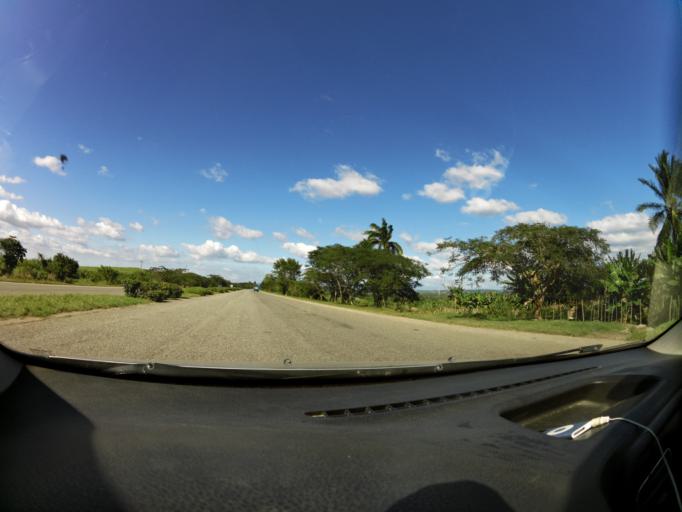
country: CU
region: Santiago de Cuba
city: San Luis
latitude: 20.1211
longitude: -75.7592
